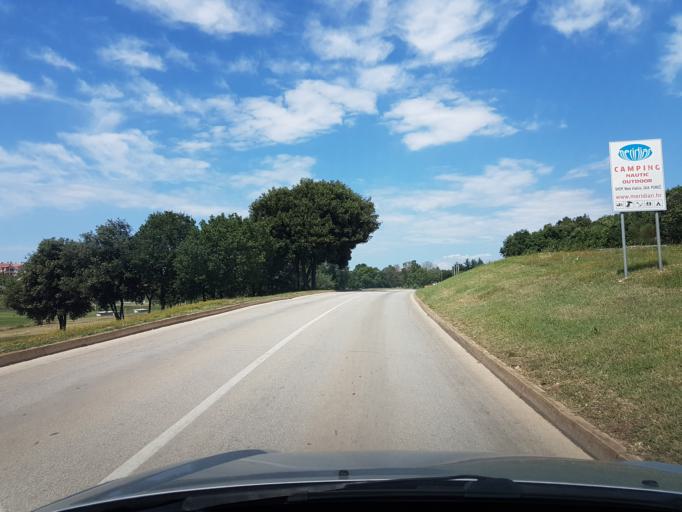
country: HR
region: Istarska
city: Vrsar
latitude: 45.1493
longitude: 13.6106
